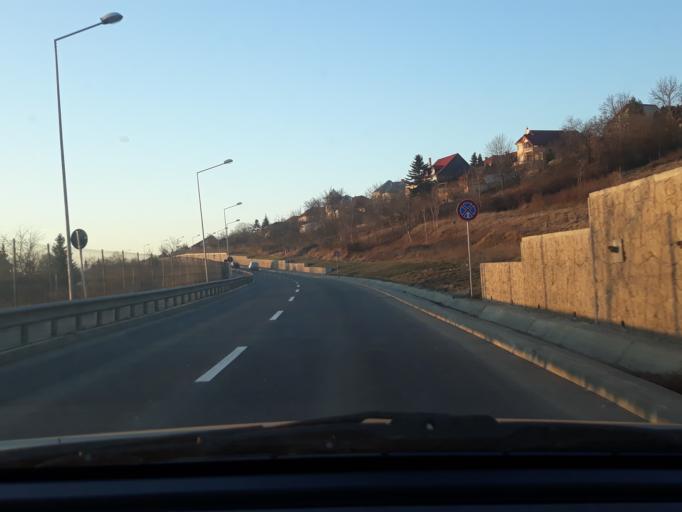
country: RO
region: Bihor
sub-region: Comuna Biharea
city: Oradea
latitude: 47.0586
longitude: 21.9475
